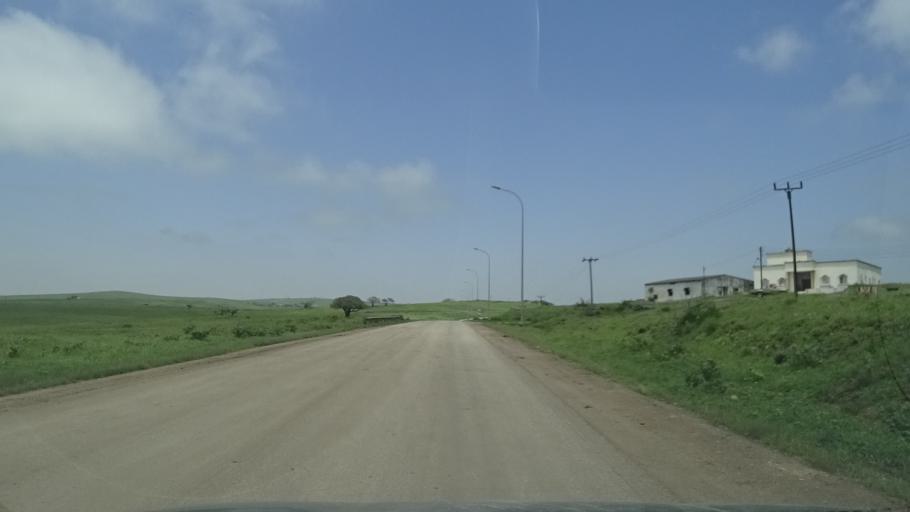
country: OM
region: Zufar
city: Salalah
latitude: 17.2153
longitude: 54.2493
